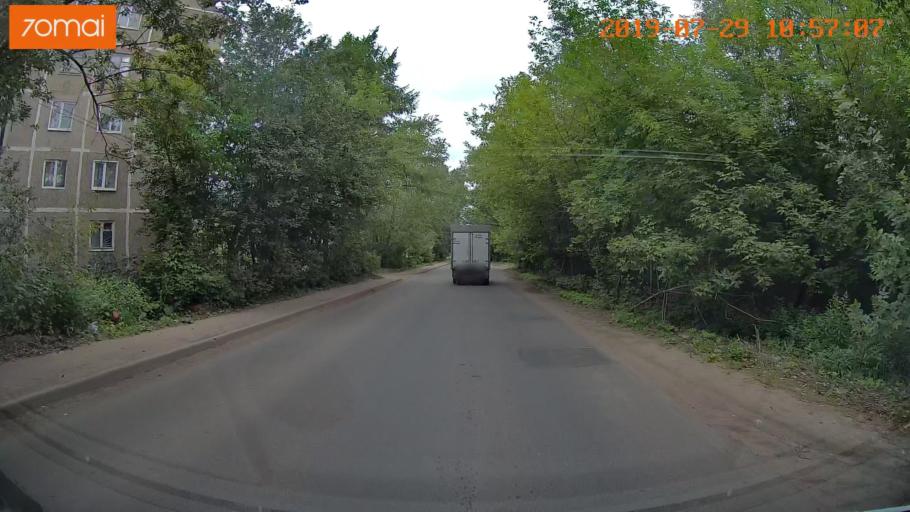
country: RU
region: Ivanovo
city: Bogorodskoye
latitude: 56.9872
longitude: 41.0347
